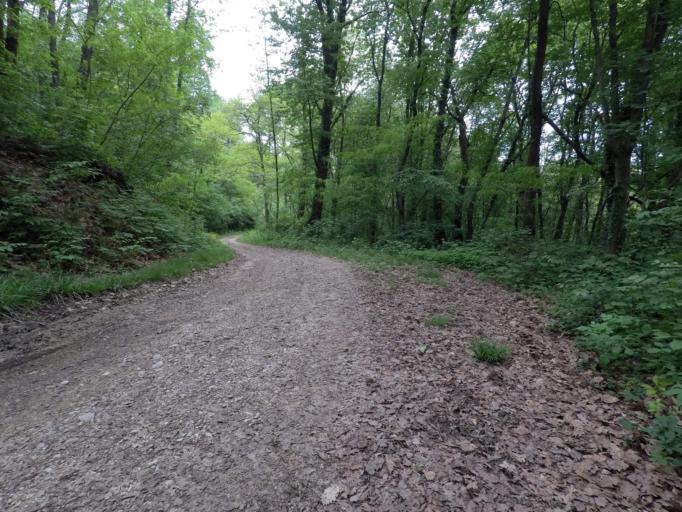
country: IT
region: Friuli Venezia Giulia
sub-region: Provincia di Udine
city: Nimis
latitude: 46.1895
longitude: 13.2394
